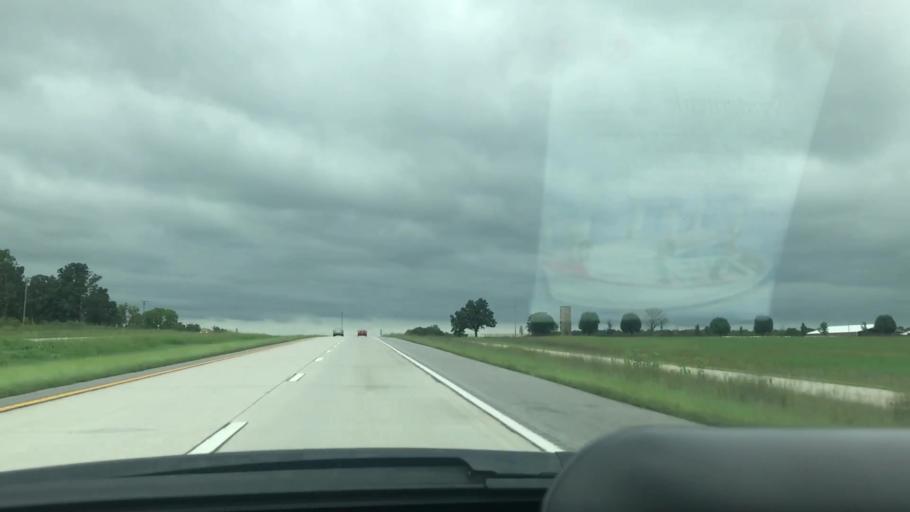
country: US
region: Missouri
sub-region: Greene County
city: Fair Grove
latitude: 37.4349
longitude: -93.1445
